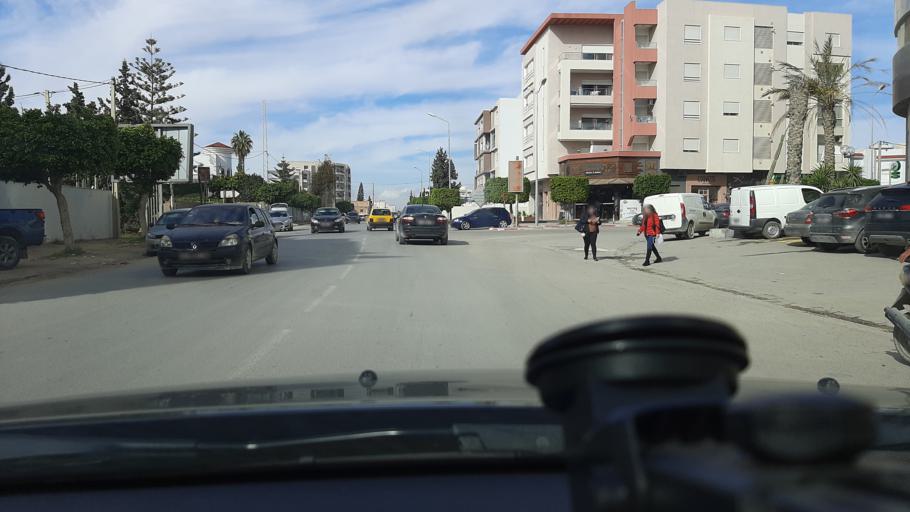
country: TN
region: Safaqis
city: Sfax
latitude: 34.7627
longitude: 10.7283
